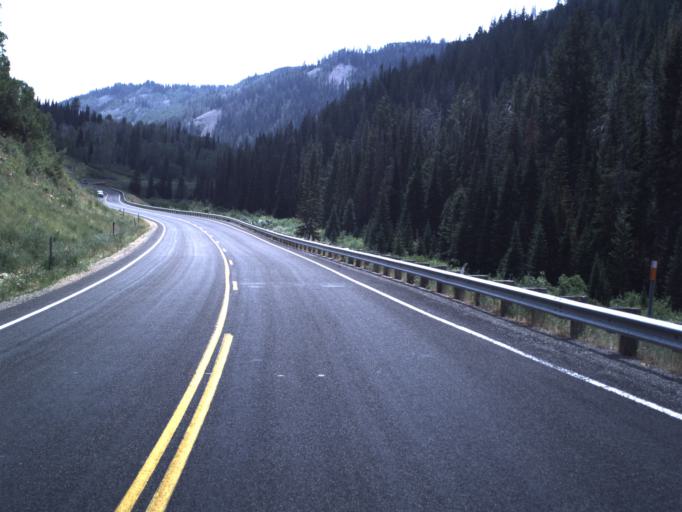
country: US
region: Utah
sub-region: Summit County
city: Francis
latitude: 40.5317
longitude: -111.0975
